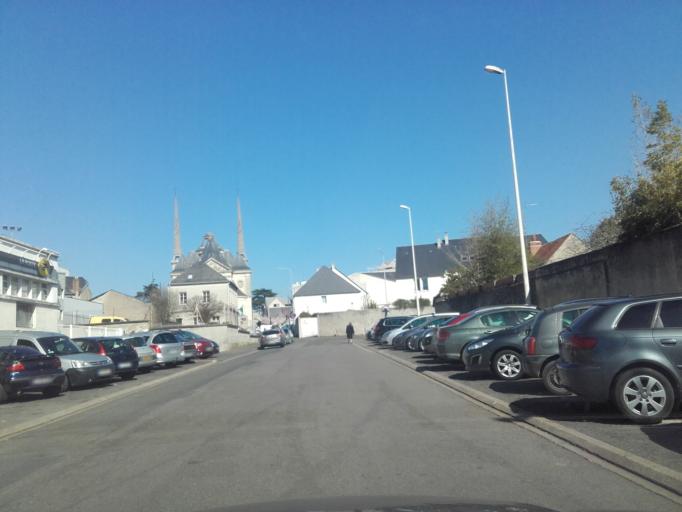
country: FR
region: Centre
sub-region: Departement d'Indre-et-Loire
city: Saint-Cyr-sur-Loire
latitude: 47.4107
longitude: 0.6850
